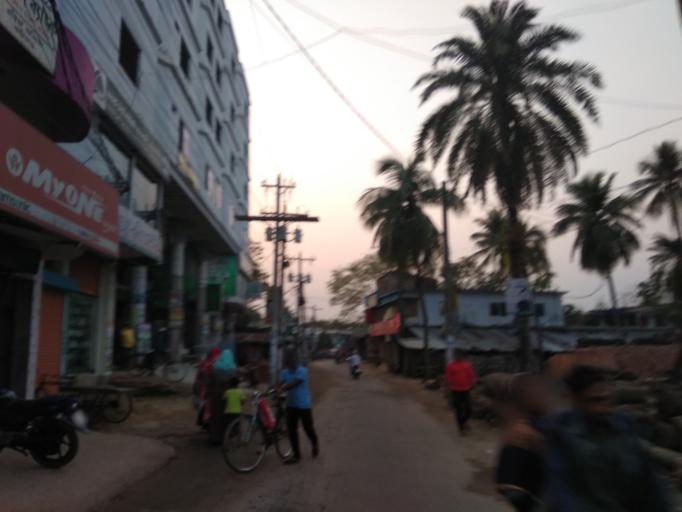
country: IN
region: West Bengal
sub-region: North 24 Parganas
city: Taki
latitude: 22.4549
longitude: 89.0326
